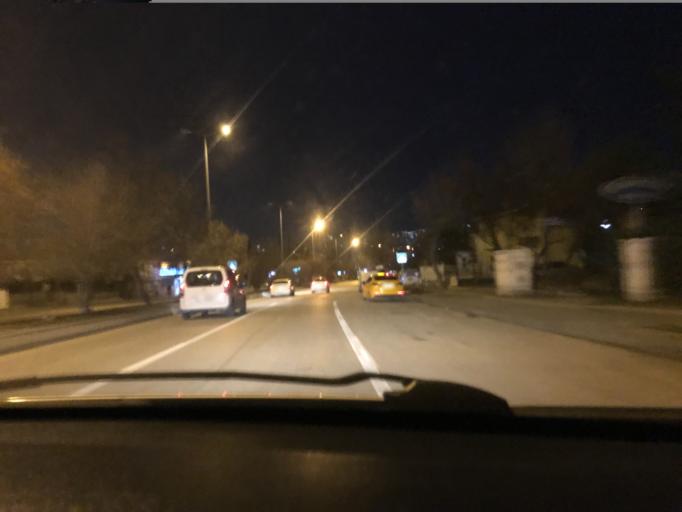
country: TR
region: Ankara
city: Batikent
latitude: 39.9530
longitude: 32.7348
